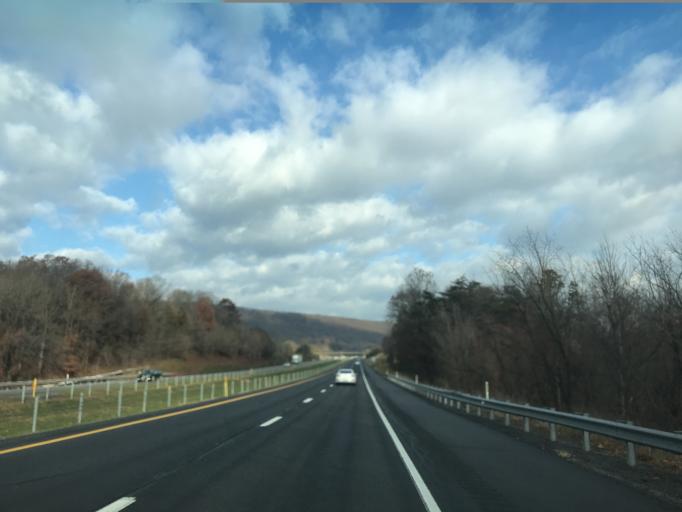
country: US
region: Maryland
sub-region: Washington County
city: Hancock
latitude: 39.8261
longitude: -78.2732
